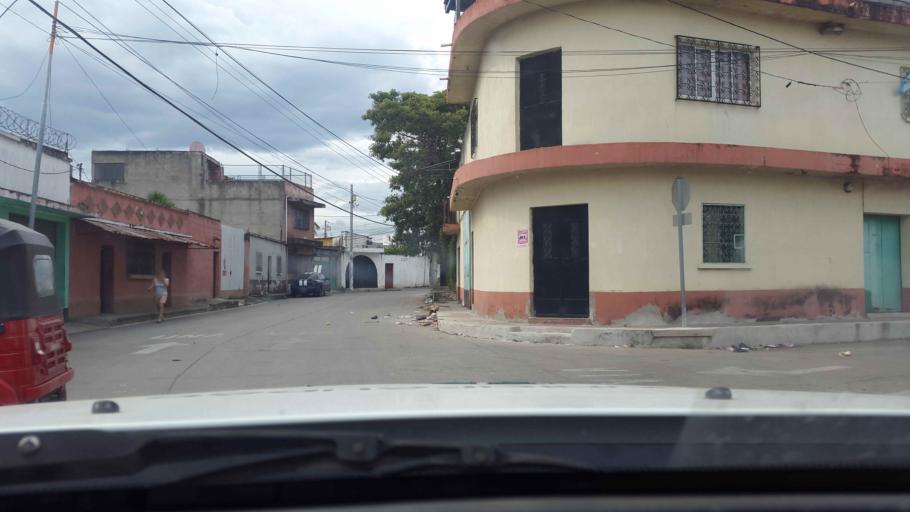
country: GT
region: Guatemala
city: Petapa
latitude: 14.5008
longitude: -90.5641
